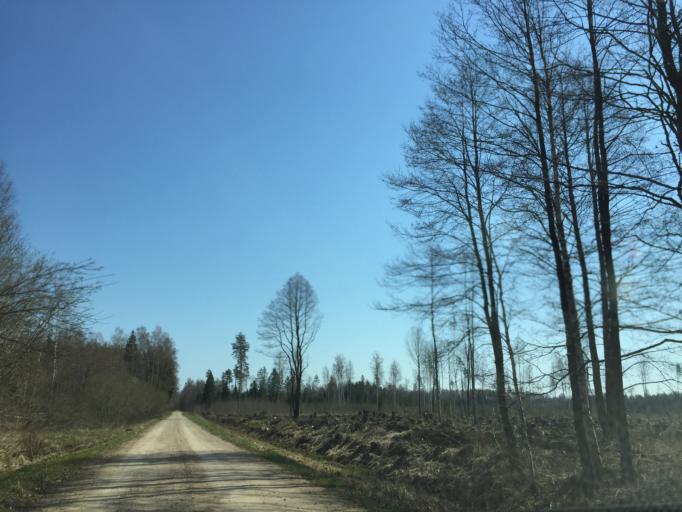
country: EE
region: Tartu
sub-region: Tartu linn
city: Tartu
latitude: 58.5294
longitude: 26.9276
